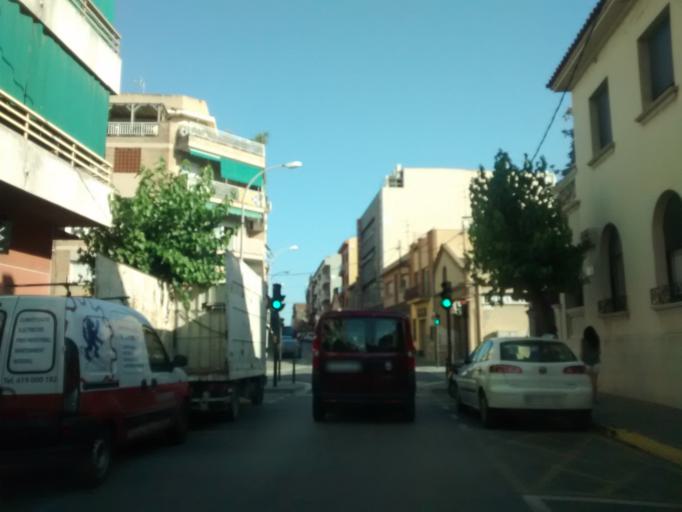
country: ES
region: Catalonia
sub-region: Provincia de Barcelona
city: Sant Vicenc dels Horts
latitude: 41.3958
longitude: 2.0084
